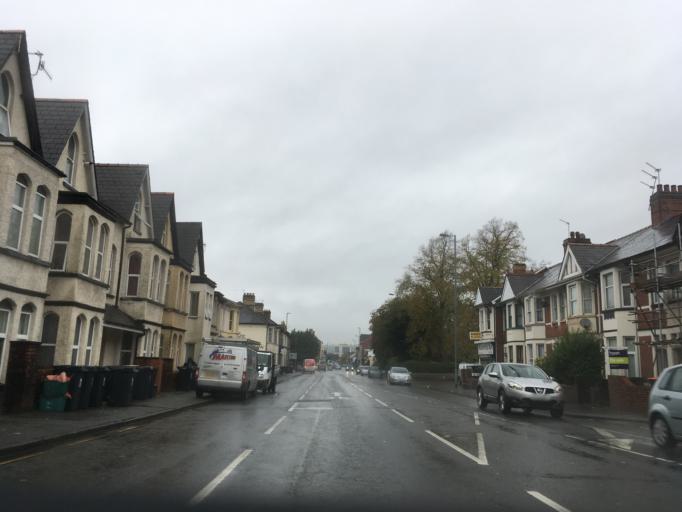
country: GB
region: Wales
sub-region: Newport
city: Newport
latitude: 51.5894
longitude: -2.9746
